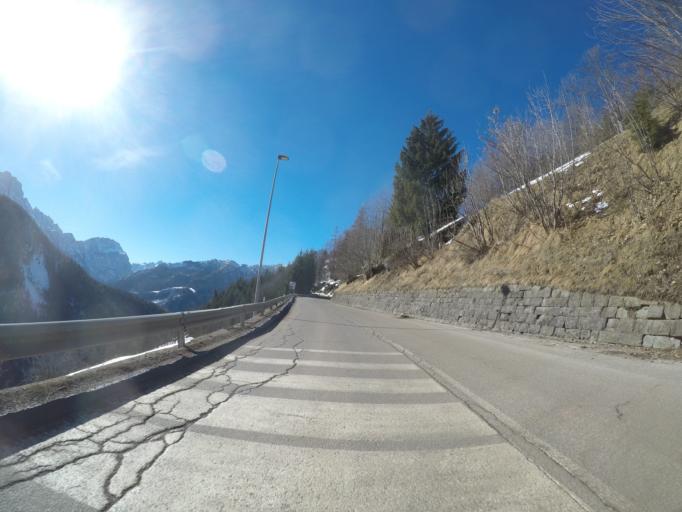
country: IT
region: Veneto
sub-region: Provincia di Belluno
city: Colle Santa Lucia
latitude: 46.4465
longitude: 12.0127
